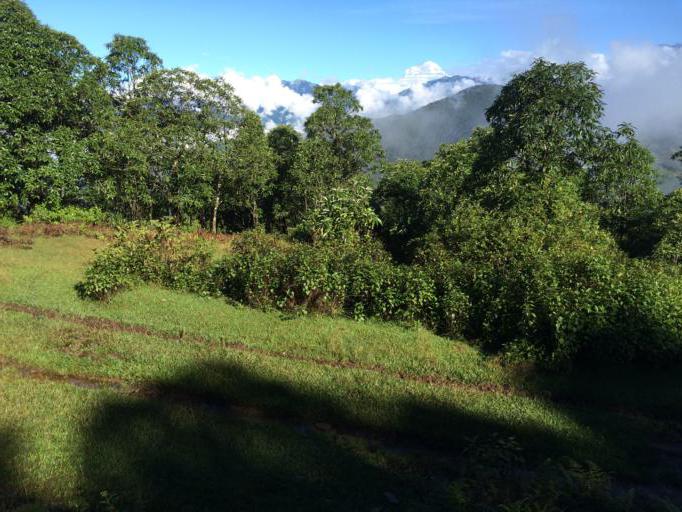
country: NP
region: Western Region
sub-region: Gandaki Zone
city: Pokhara
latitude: 28.2540
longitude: 83.8226
